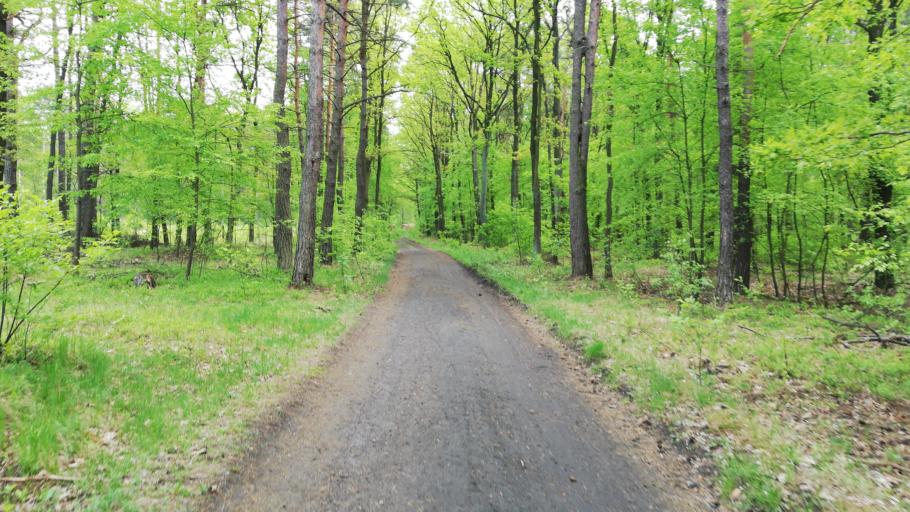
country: PL
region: Silesian Voivodeship
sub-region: Ruda Slaska
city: Ruda Slaska
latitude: 50.2526
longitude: 18.8196
